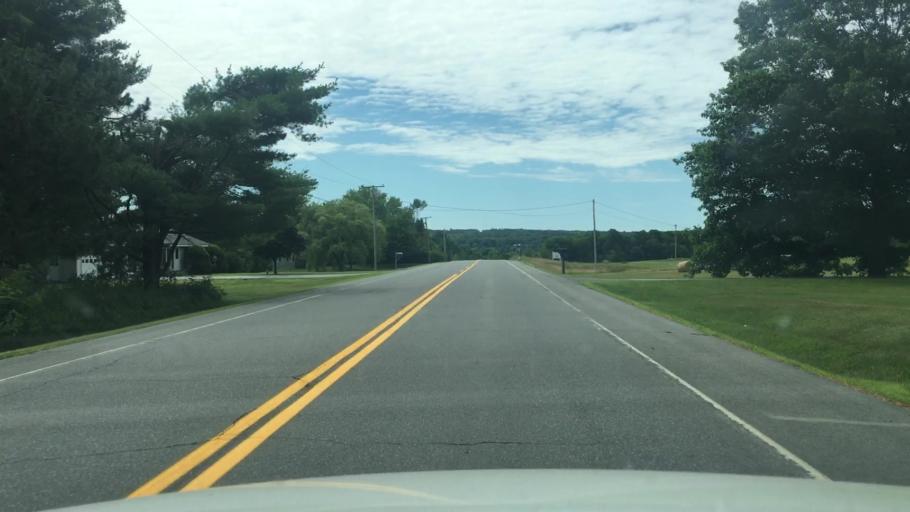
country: US
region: Maine
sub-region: Waldo County
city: Troy
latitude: 44.5876
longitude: -69.2806
